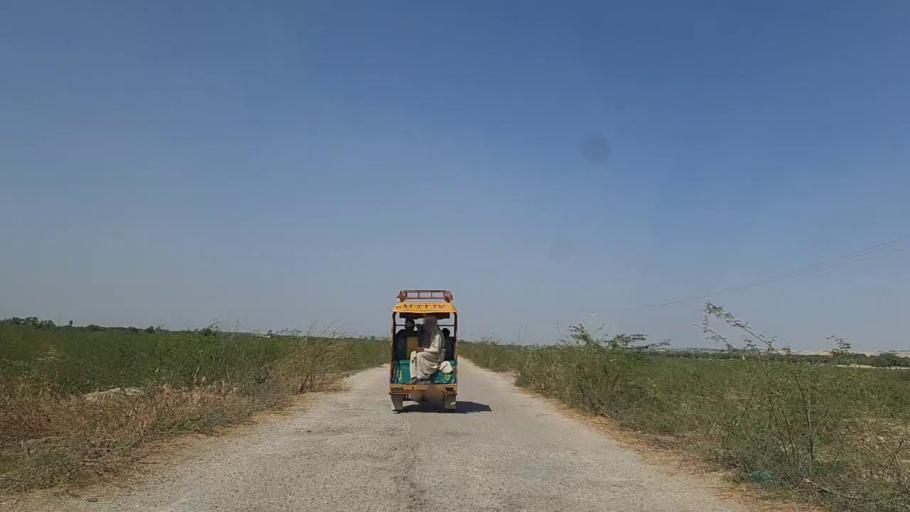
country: PK
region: Sindh
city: Naukot
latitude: 24.6428
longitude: 69.2879
